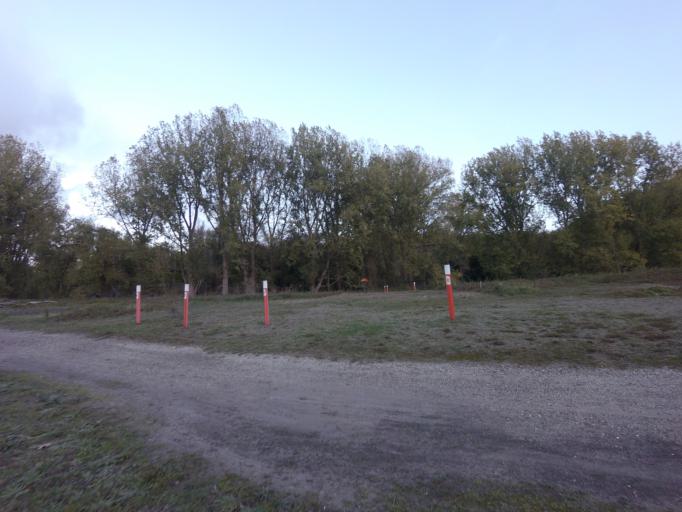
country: BE
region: Flanders
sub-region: Provincie Antwerpen
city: Zwijndrecht
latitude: 51.2339
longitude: 4.3605
